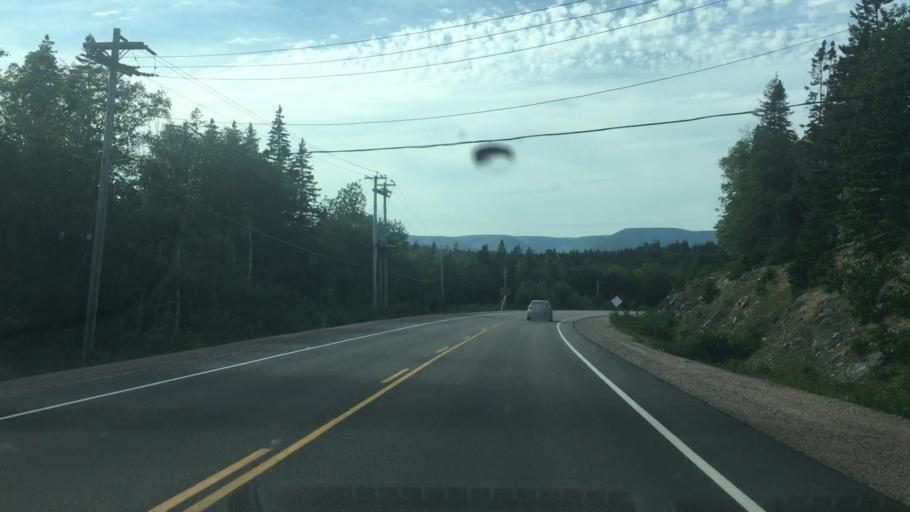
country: CA
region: Nova Scotia
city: Sydney Mines
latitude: 46.8572
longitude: -60.4615
